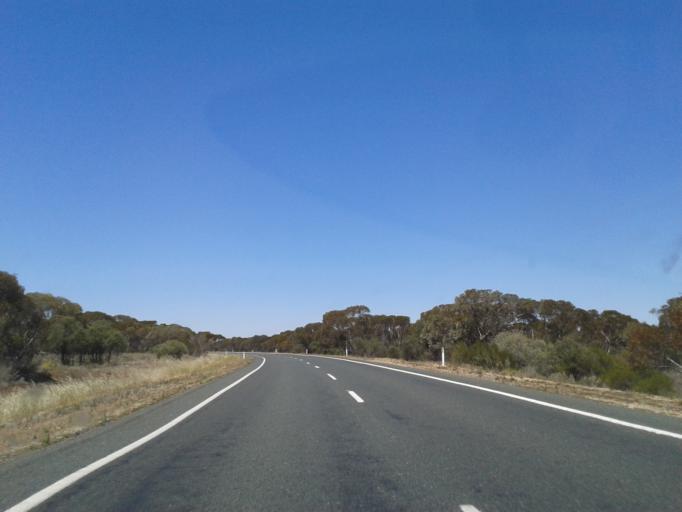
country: AU
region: New South Wales
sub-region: Wentworth
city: Gol Gol
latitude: -34.5308
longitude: 142.6258
